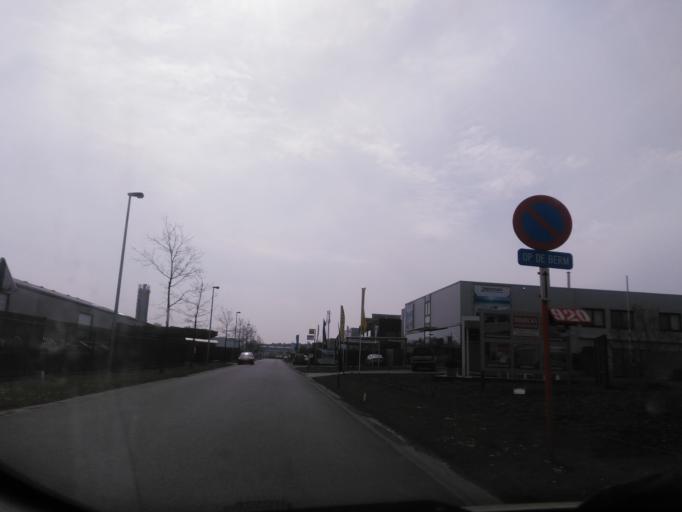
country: BE
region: Flanders
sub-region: Provincie Oost-Vlaanderen
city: Beveren
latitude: 51.2002
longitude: 4.2148
